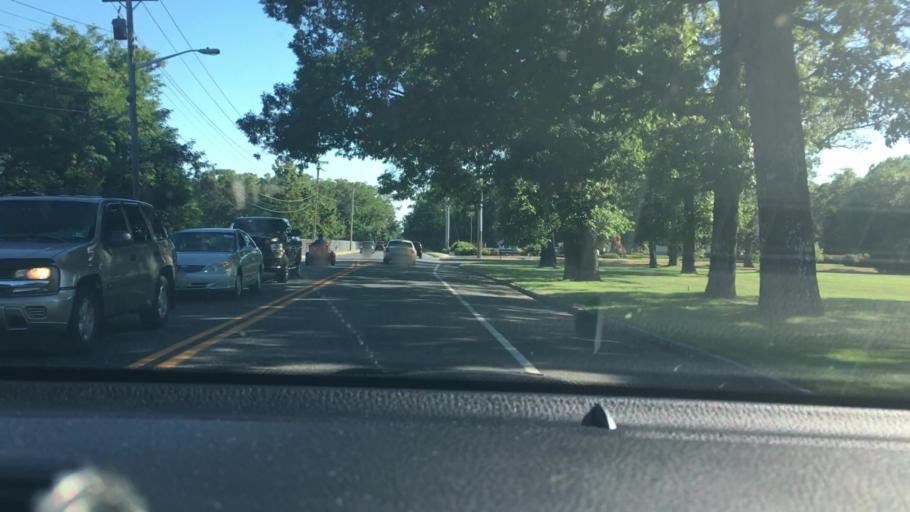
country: US
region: New Jersey
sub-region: Cumberland County
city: Millville
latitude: 39.4169
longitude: -75.0410
